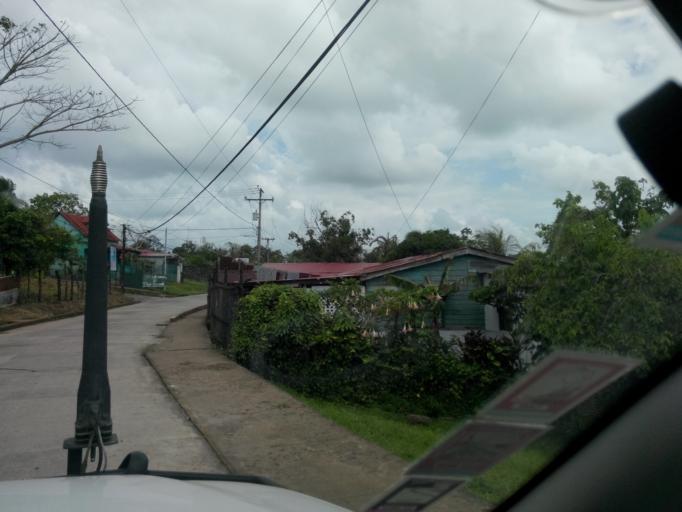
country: NI
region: Atlantico Sur
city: Bluefields
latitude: 12.0177
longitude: -83.7623
